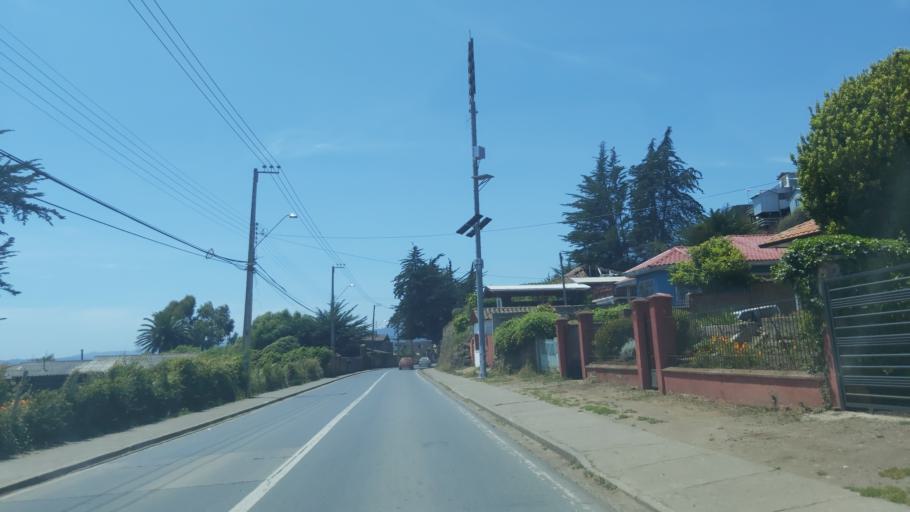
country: CL
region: Maule
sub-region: Provincia de Cauquenes
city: Cauquenes
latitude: -35.8160
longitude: -72.5828
